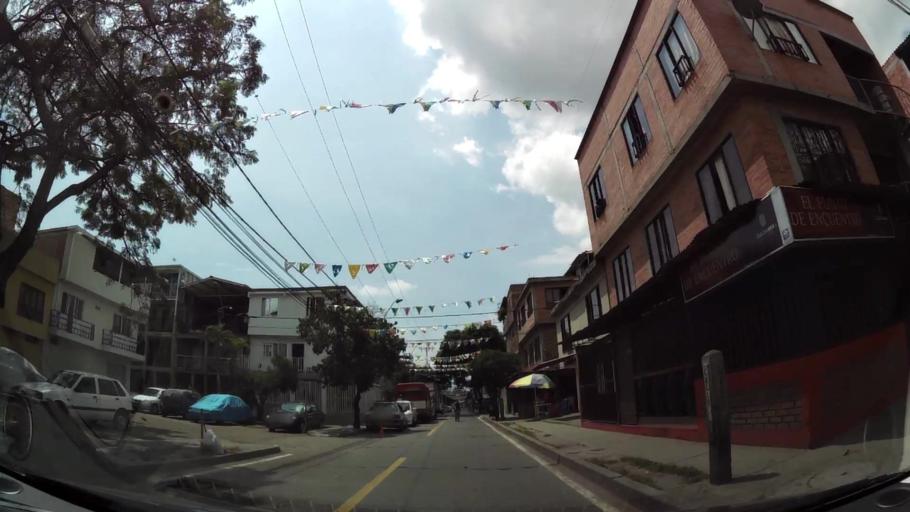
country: CO
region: Valle del Cauca
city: Cali
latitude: 3.4884
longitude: -76.4849
